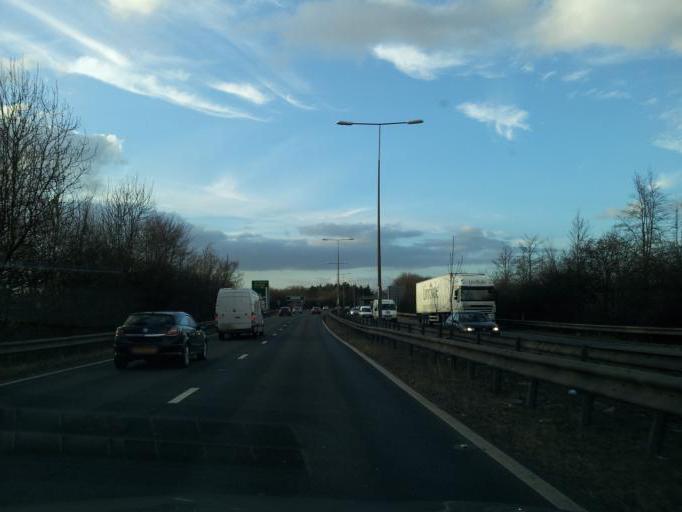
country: GB
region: England
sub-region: District of Rutland
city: Clipsham
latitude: 52.8110
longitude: -0.6169
